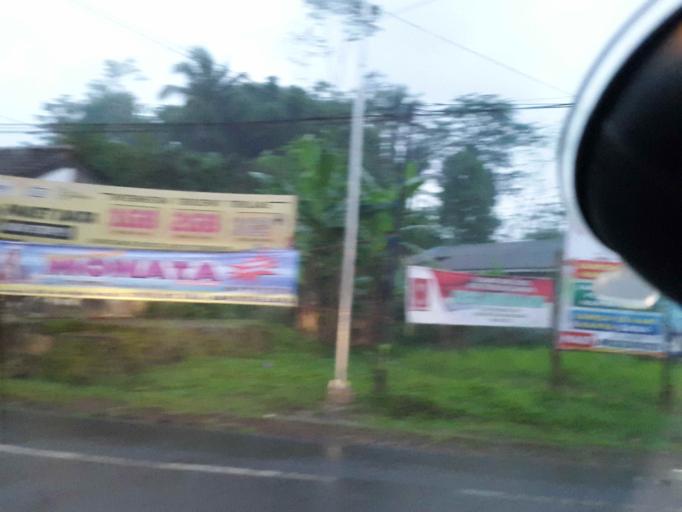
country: ID
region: Central Java
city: Wonosobo
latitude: -7.3605
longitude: 109.6880
